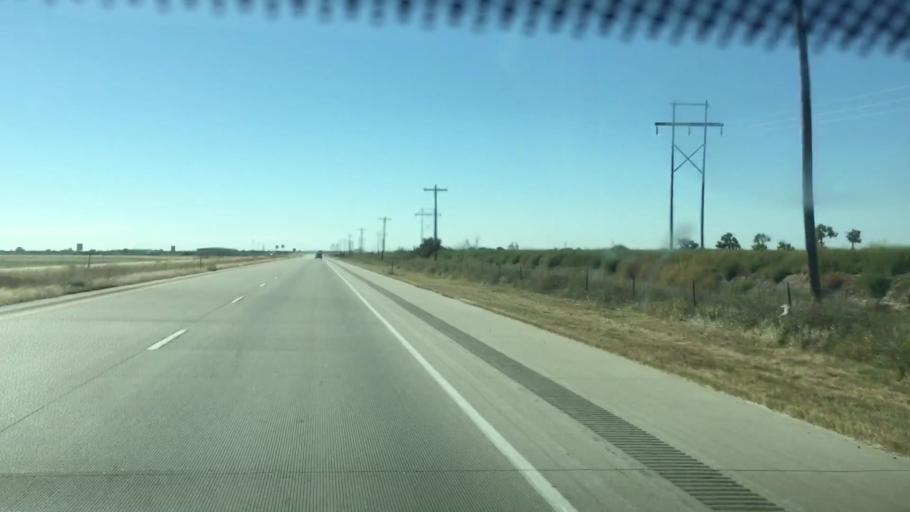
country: US
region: Colorado
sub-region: Prowers County
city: Lamar
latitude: 38.1097
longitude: -102.6836
